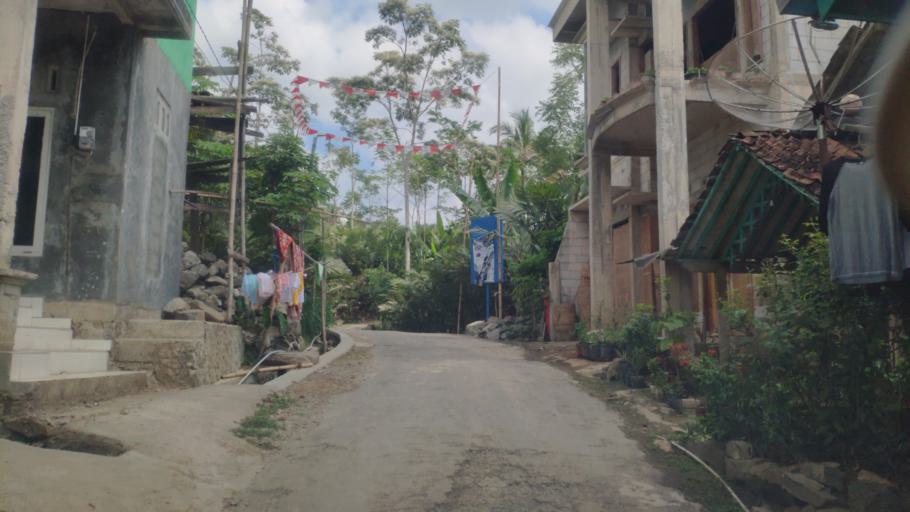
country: ID
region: Central Java
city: Wonosobo
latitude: -7.3381
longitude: 109.7854
